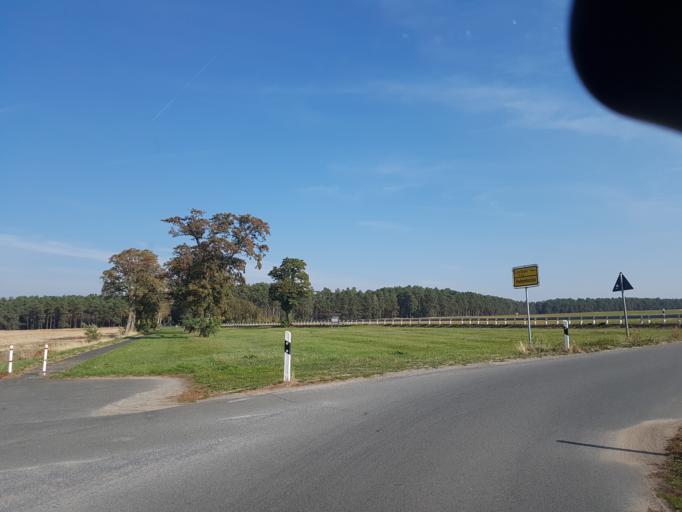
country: DE
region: Brandenburg
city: Hohenbucko
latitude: 51.7703
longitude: 13.4742
